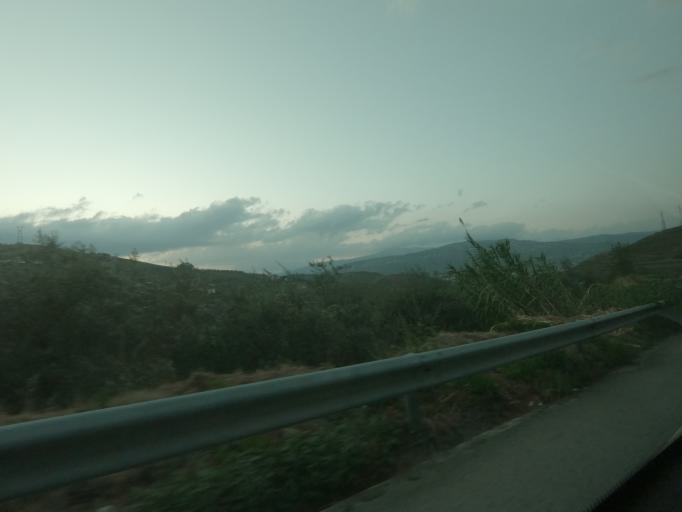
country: PT
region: Vila Real
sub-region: Peso da Regua
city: Peso da Regua
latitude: 41.1452
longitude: -7.7756
